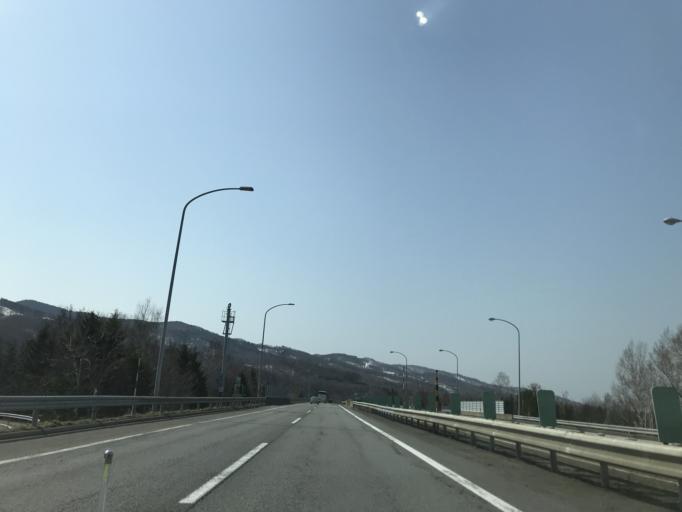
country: JP
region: Hokkaido
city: Bibai
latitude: 43.3338
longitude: 141.8882
